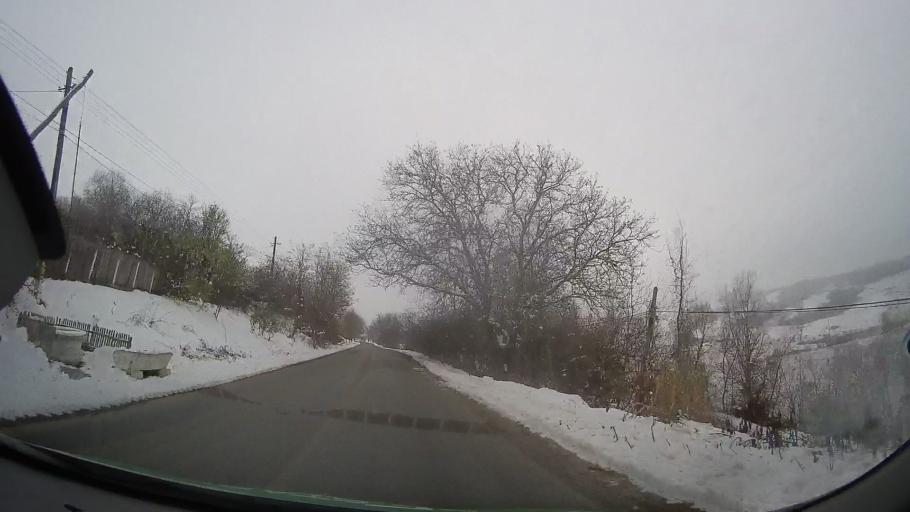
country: RO
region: Bacau
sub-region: Comuna Vultureni
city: Vultureni
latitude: 46.3842
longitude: 27.2770
